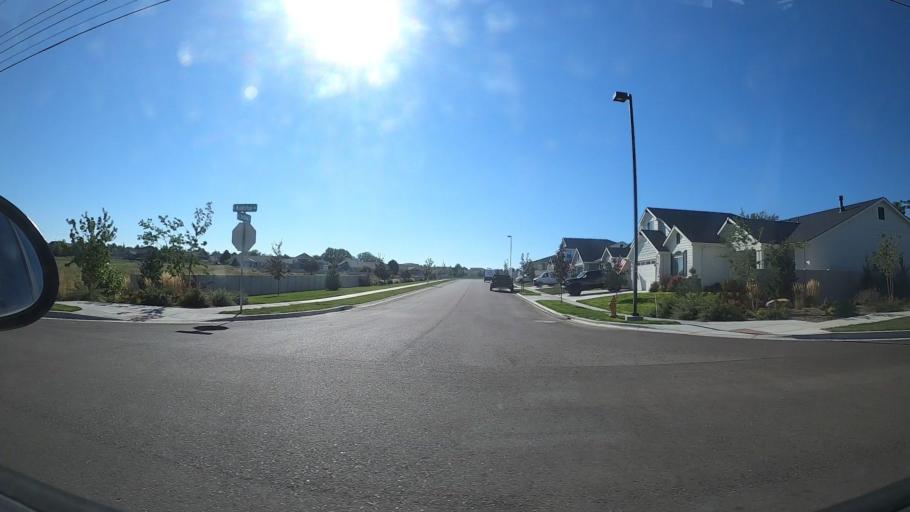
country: US
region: Idaho
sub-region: Canyon County
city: Nampa
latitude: 43.5585
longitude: -116.6128
